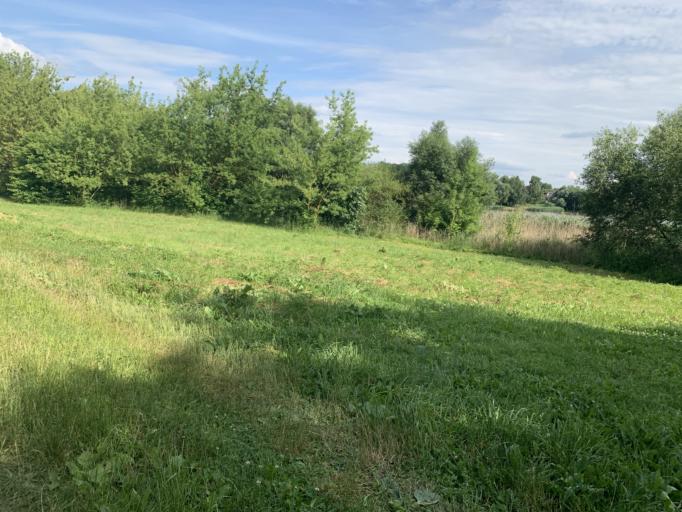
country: BY
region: Minsk
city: Nyasvizh
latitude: 53.2137
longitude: 26.6812
